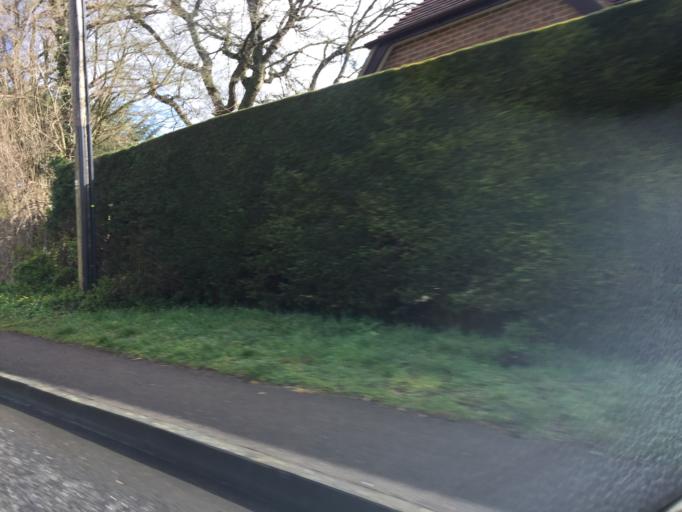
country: GB
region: England
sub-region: Hampshire
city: Compton
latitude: 51.0145
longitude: -1.3393
